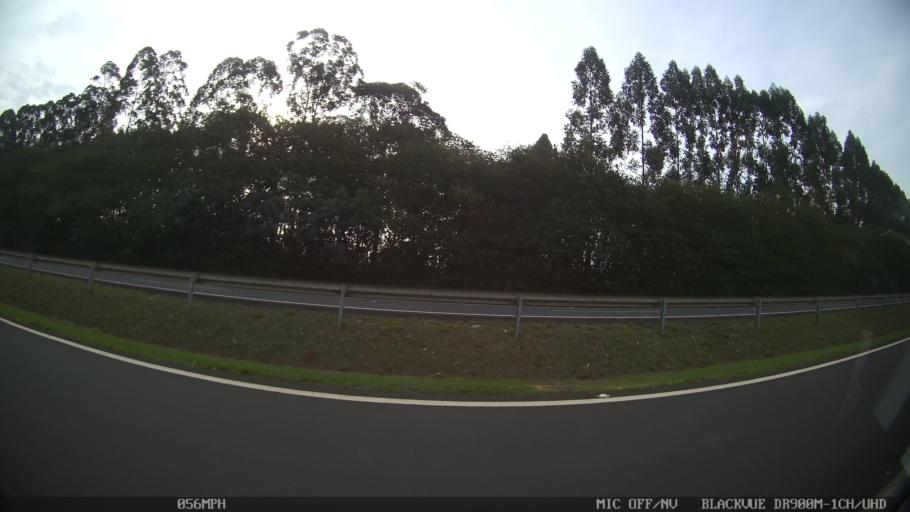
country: BR
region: Sao Paulo
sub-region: Iracemapolis
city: Iracemapolis
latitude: -22.6580
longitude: -47.5226
